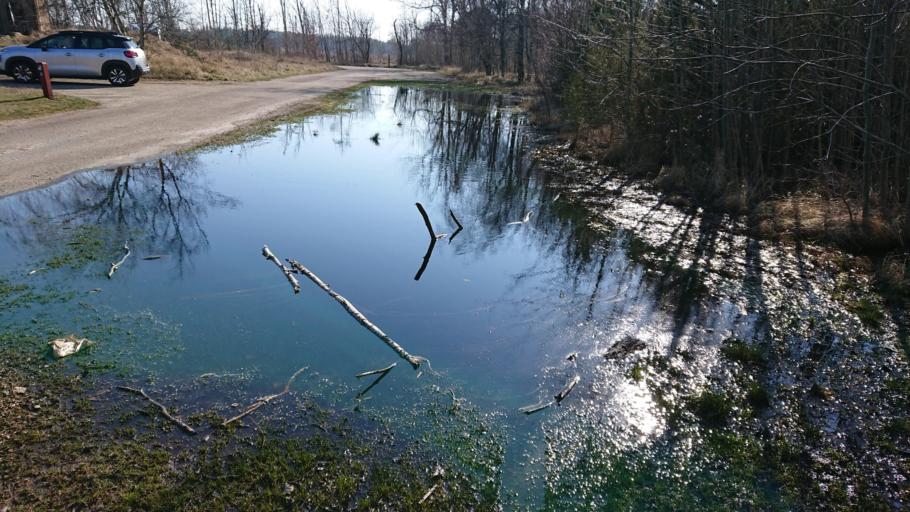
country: DK
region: North Denmark
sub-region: Frederikshavn Kommune
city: Skagen
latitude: 57.7142
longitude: 10.5431
